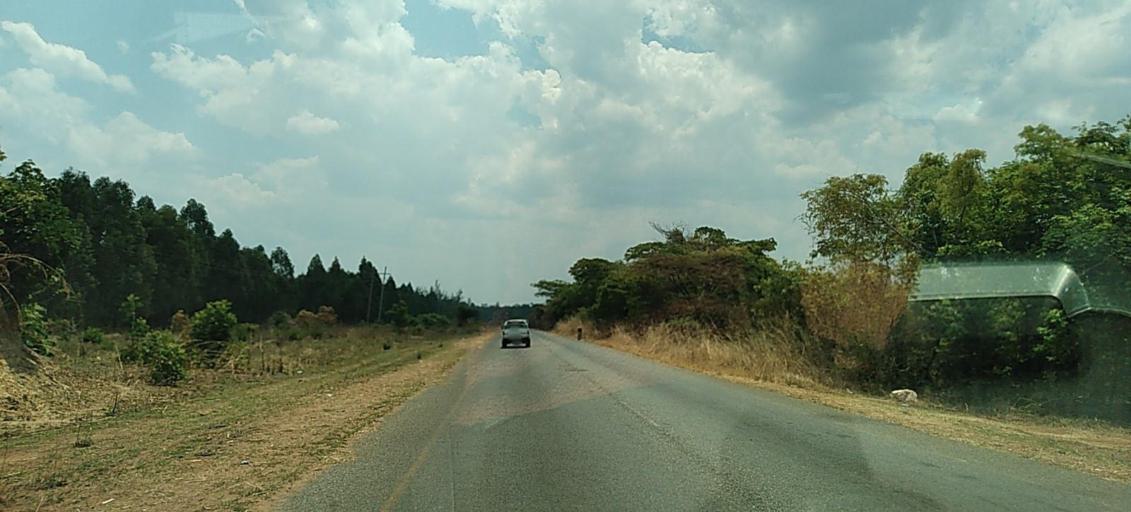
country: ZM
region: Copperbelt
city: Kalulushi
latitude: -12.8375
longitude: 27.9321
